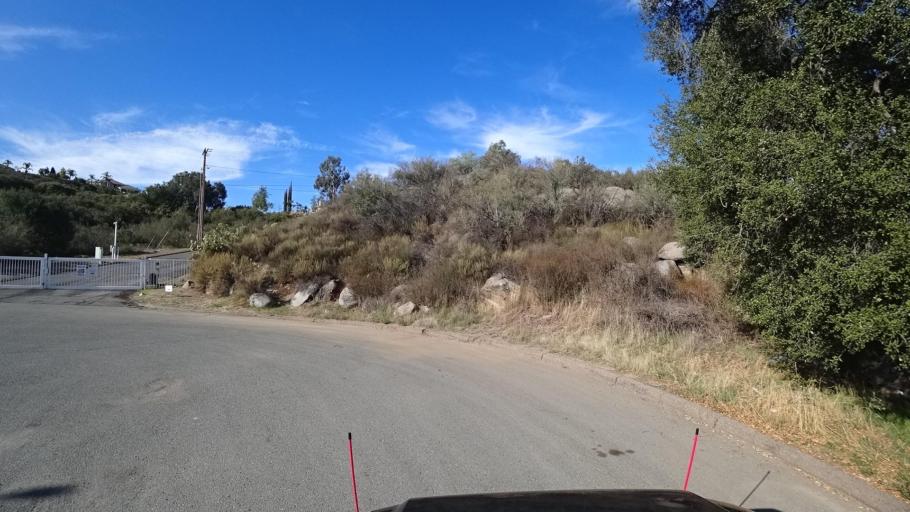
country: US
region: California
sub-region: San Diego County
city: Alpine
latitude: 32.8125
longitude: -116.7466
